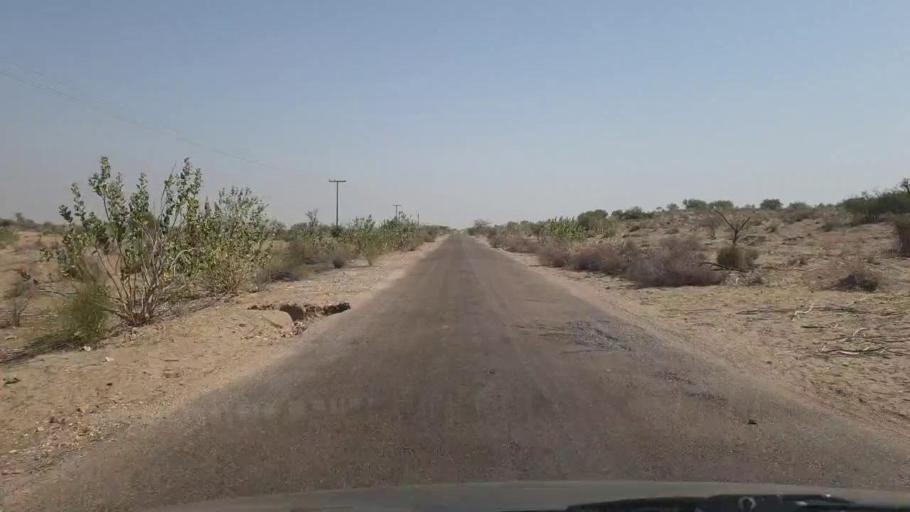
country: PK
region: Sindh
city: Chor
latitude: 25.5852
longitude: 69.9377
